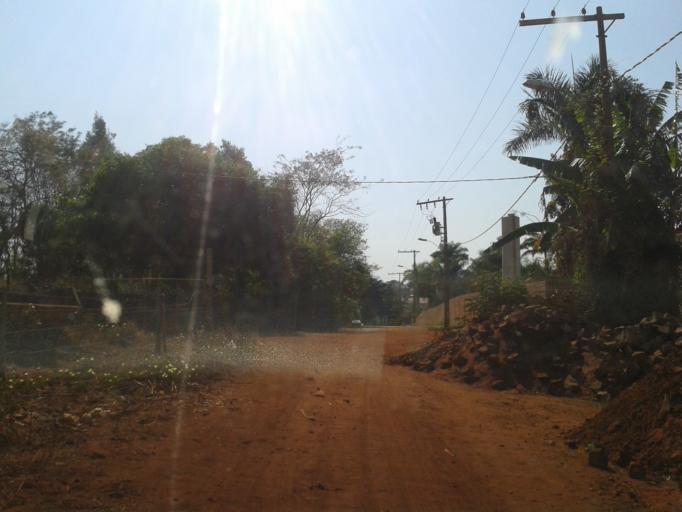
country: BR
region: Minas Gerais
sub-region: Ituiutaba
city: Ituiutaba
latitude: -18.9651
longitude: -49.4762
